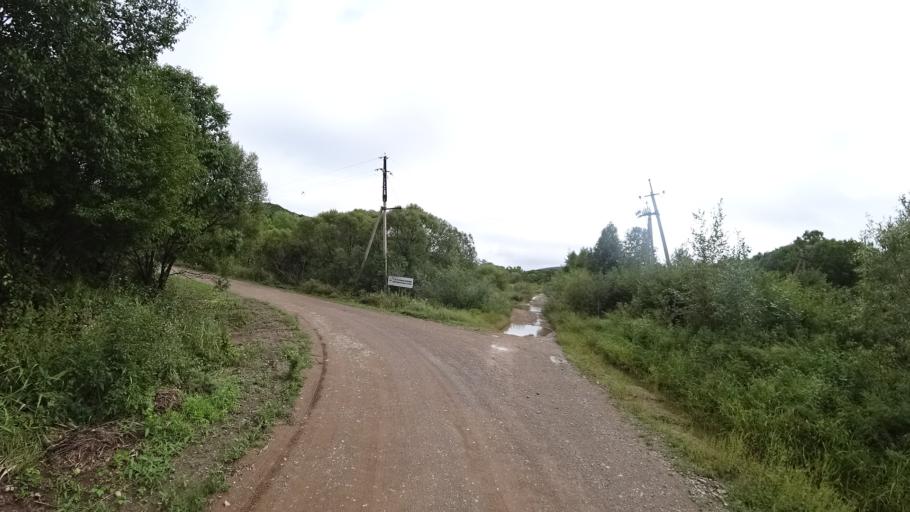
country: RU
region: Primorskiy
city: Monastyrishche
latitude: 44.1642
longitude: 132.5381
